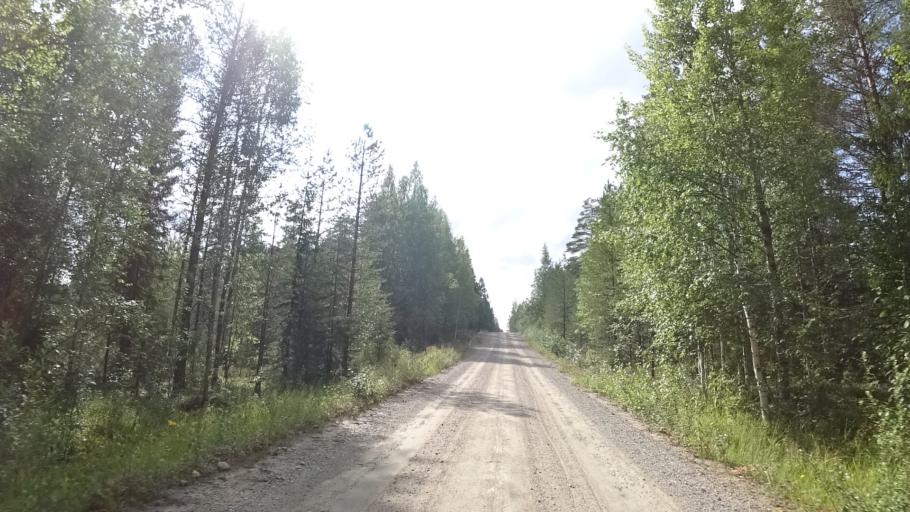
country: FI
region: North Karelia
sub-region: Joensuu
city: Ilomantsi
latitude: 62.9241
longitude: 31.3570
